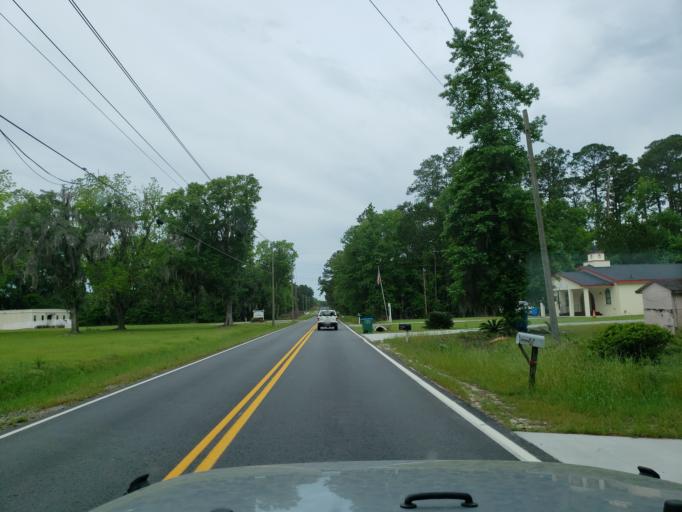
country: US
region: Georgia
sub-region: Chatham County
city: Port Wentworth
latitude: 32.1801
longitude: -81.1970
